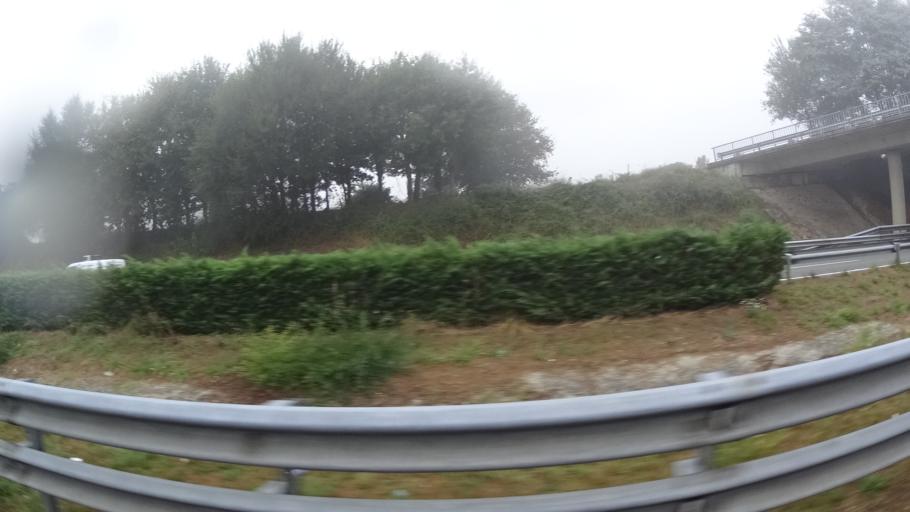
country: ES
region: Galicia
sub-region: Provincia de Lugo
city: Lugo
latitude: 42.9814
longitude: -7.5013
